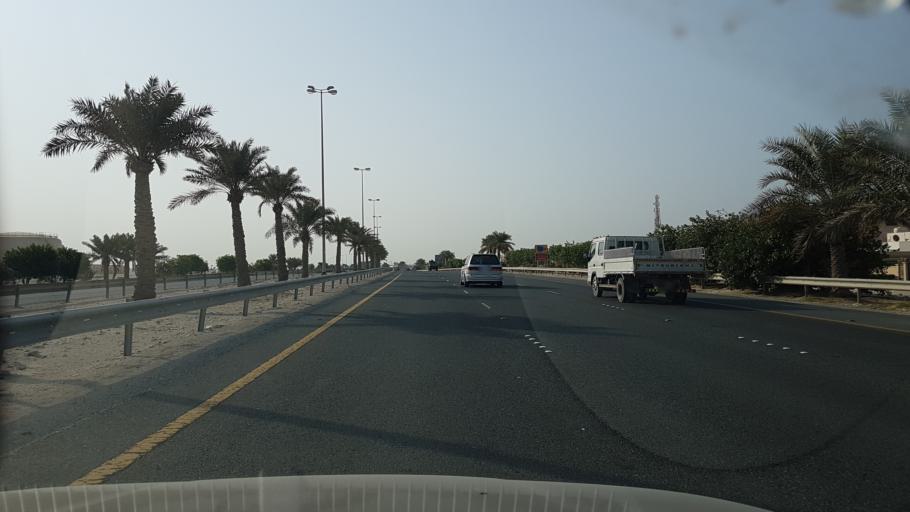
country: BH
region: Central Governorate
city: Dar Kulayb
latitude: 26.0747
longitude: 50.5146
